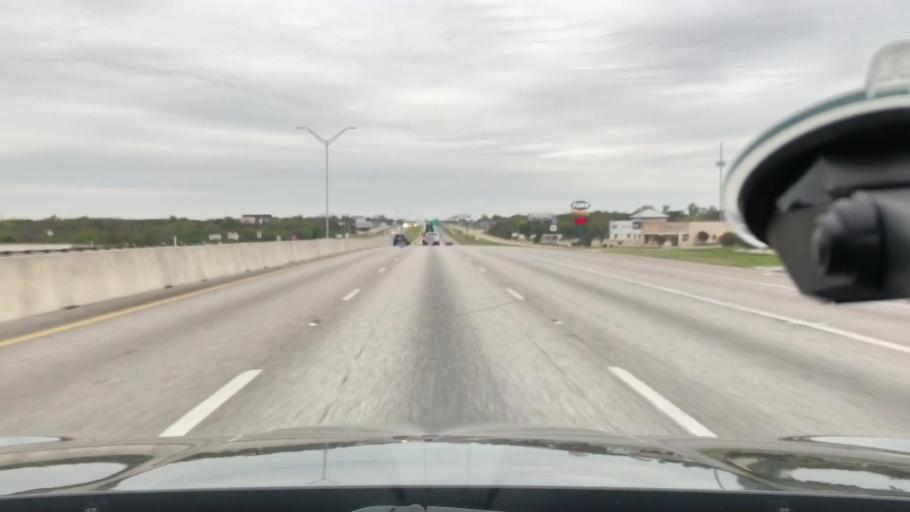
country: US
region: Texas
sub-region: McLennan County
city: Bellmead
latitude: 31.6075
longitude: -97.1049
